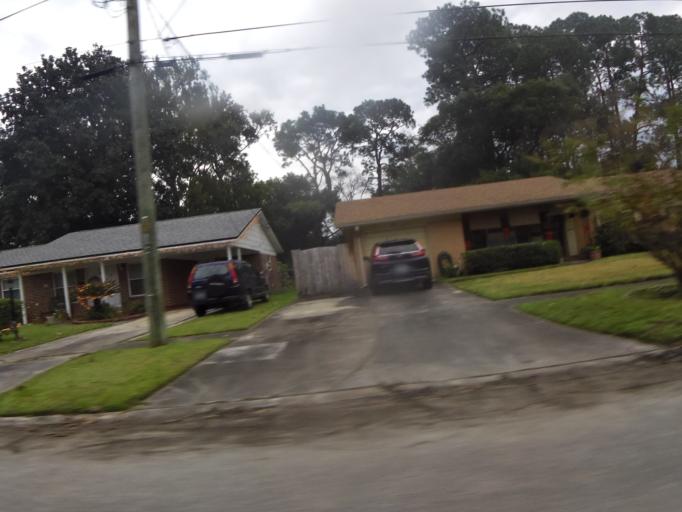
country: US
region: Florida
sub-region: Duval County
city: Jacksonville
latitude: 30.2666
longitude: -81.5969
